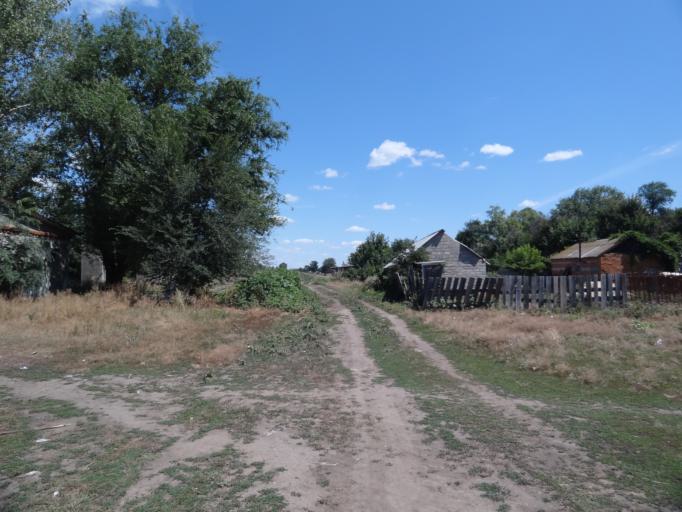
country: RU
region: Saratov
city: Sovetskoye
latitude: 51.2825
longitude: 46.6408
